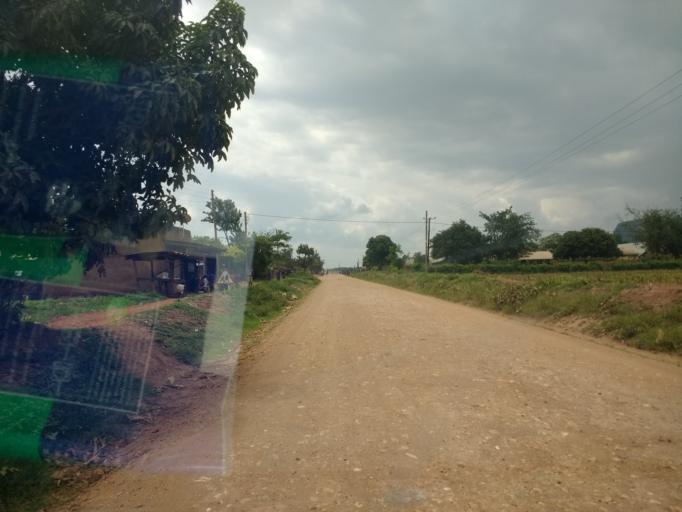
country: UG
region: Eastern Region
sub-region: Sironko District
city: Sironko
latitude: 1.3392
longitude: 34.2994
